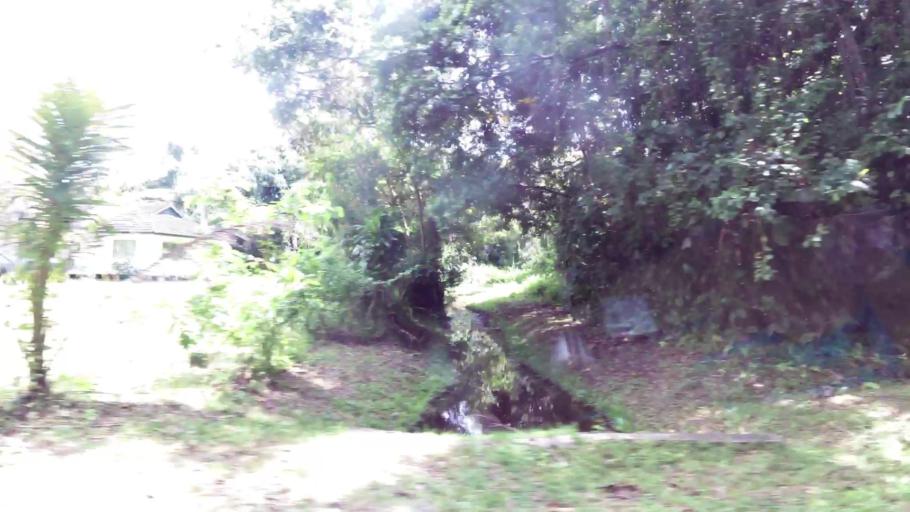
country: BN
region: Belait
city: Kuala Belait
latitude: 4.5950
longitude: 114.2599
